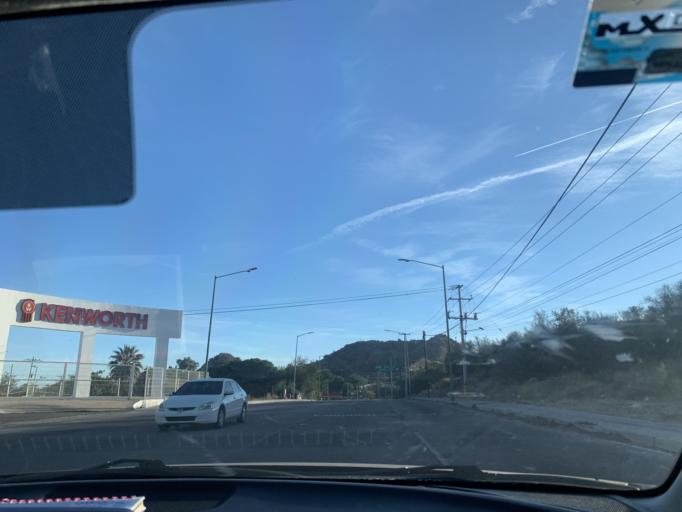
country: MX
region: Sonora
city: Hermosillo
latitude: 29.0907
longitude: -110.9312
